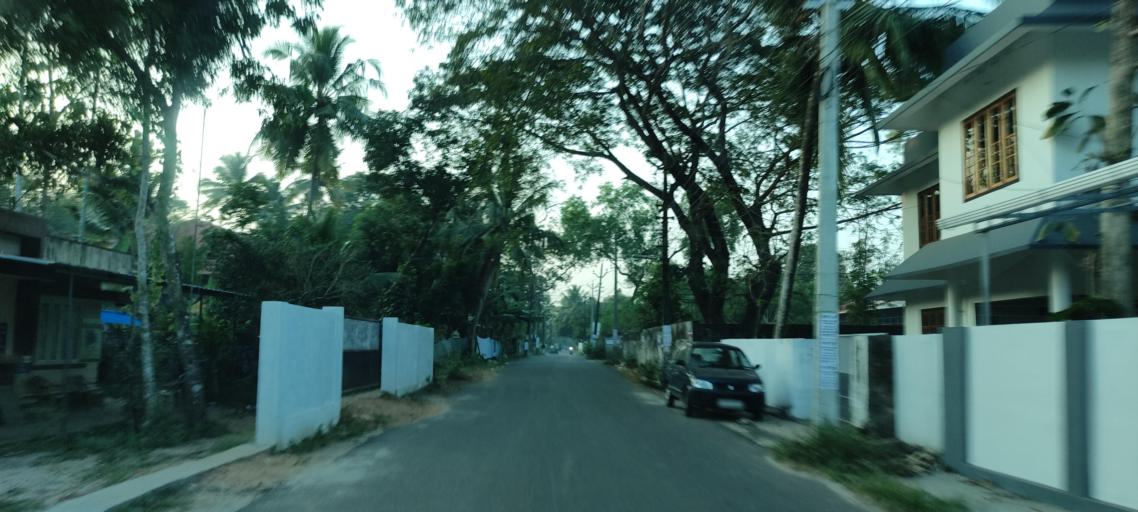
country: IN
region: Kerala
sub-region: Alappuzha
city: Alleppey
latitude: 9.4287
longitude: 76.3478
